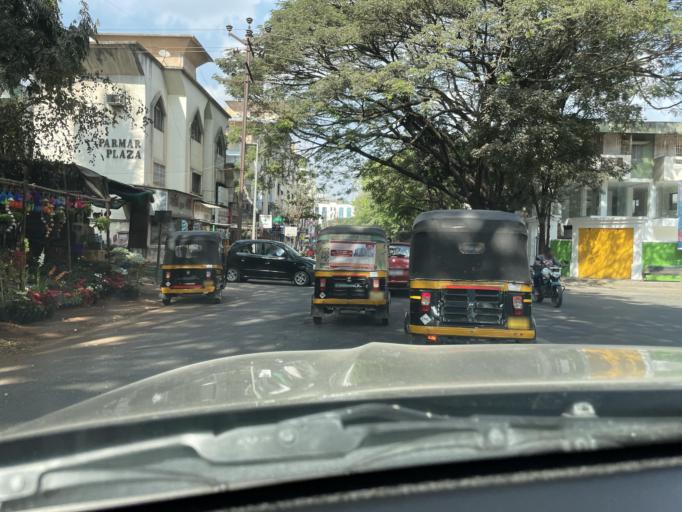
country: IN
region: Maharashtra
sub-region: Pune Division
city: Pune
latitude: 18.5007
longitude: 73.9005
